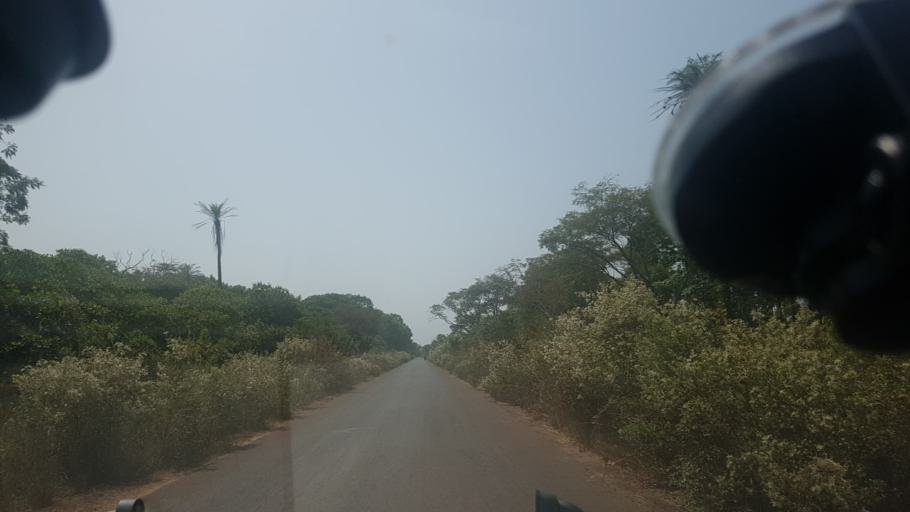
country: GW
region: Cacheu
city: Cacheu
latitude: 12.4099
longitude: -16.0318
